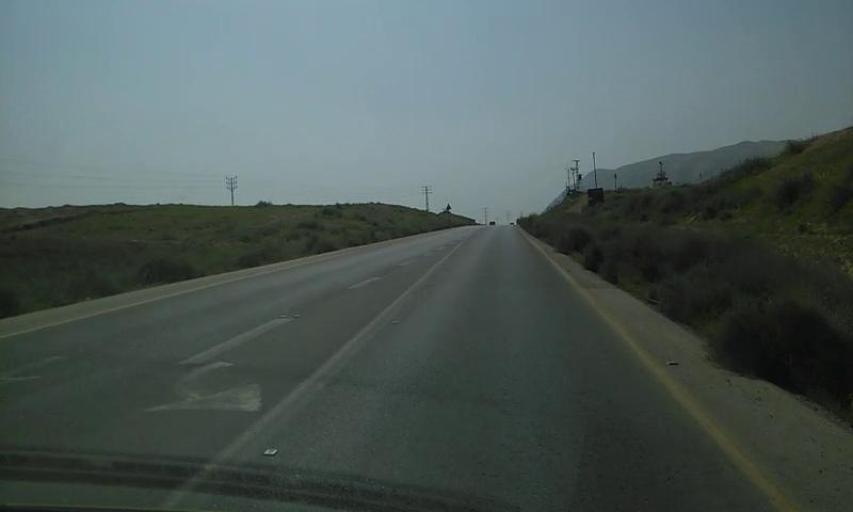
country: PS
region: West Bank
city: An Nuway`imah
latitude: 31.9058
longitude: 35.4238
